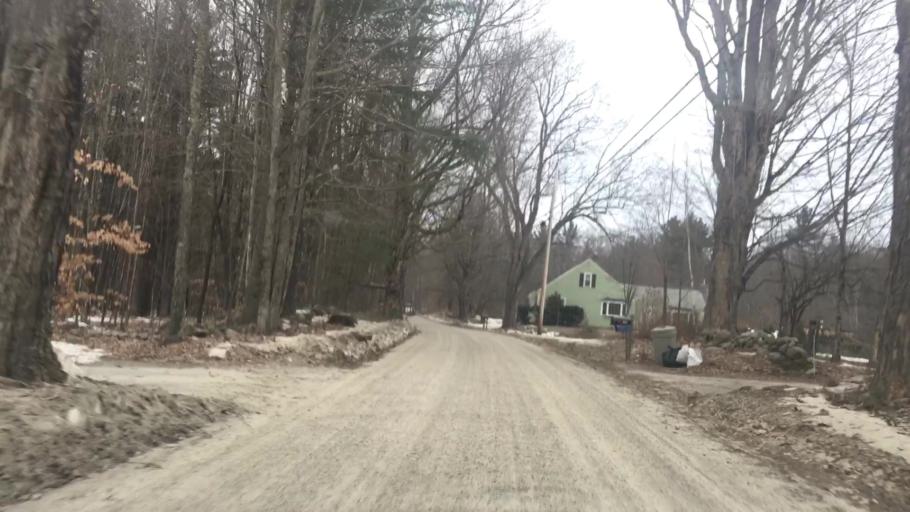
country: US
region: New Hampshire
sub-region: Merrimack County
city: Hopkinton
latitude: 43.1639
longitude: -71.6682
